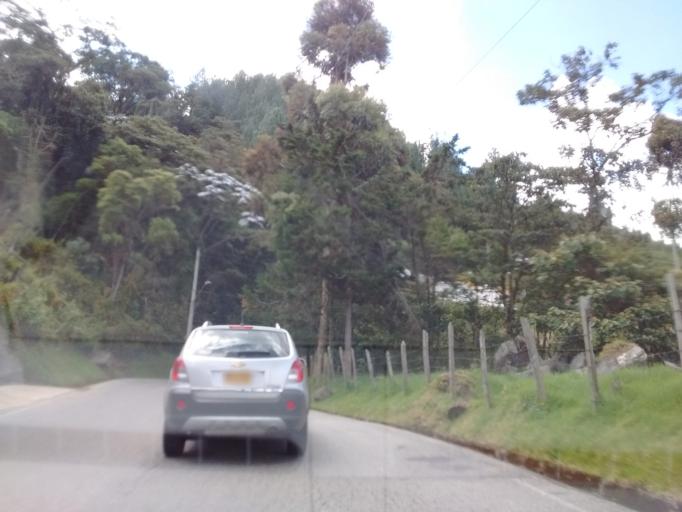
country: CO
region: Antioquia
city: Medellin
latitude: 6.2398
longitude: -75.5115
